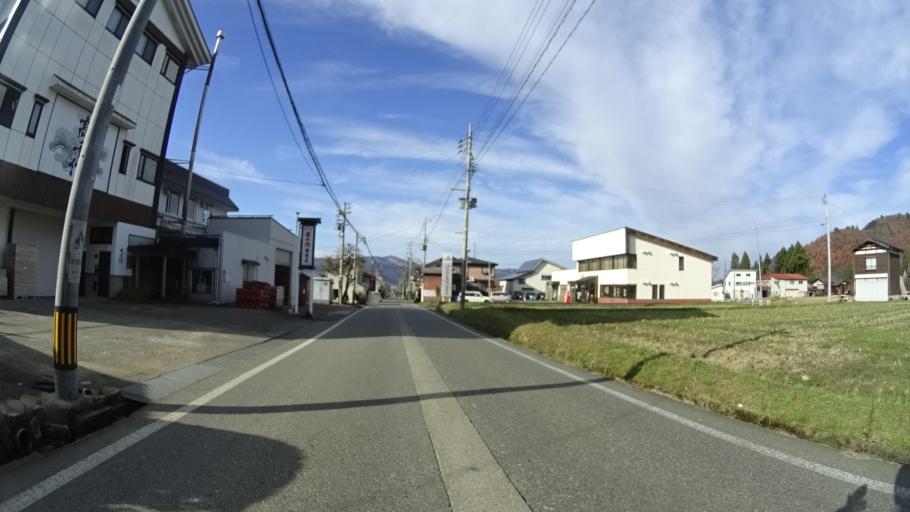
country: JP
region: Niigata
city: Shiozawa
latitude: 37.0157
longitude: 138.8788
